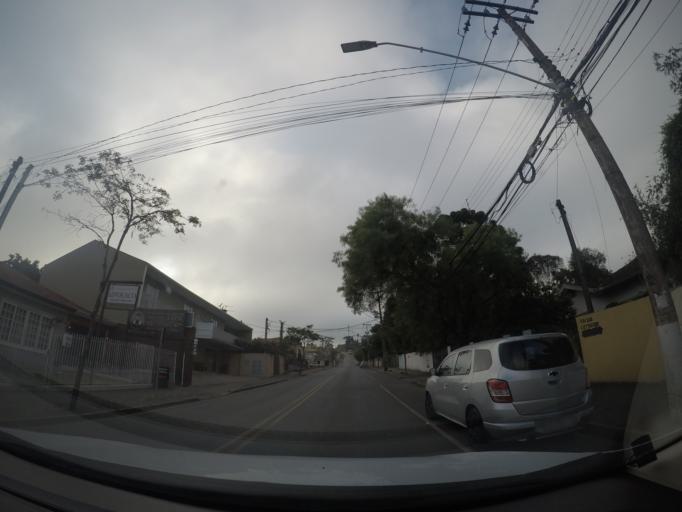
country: BR
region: Parana
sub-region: Colombo
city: Colombo
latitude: -25.2933
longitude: -49.2250
